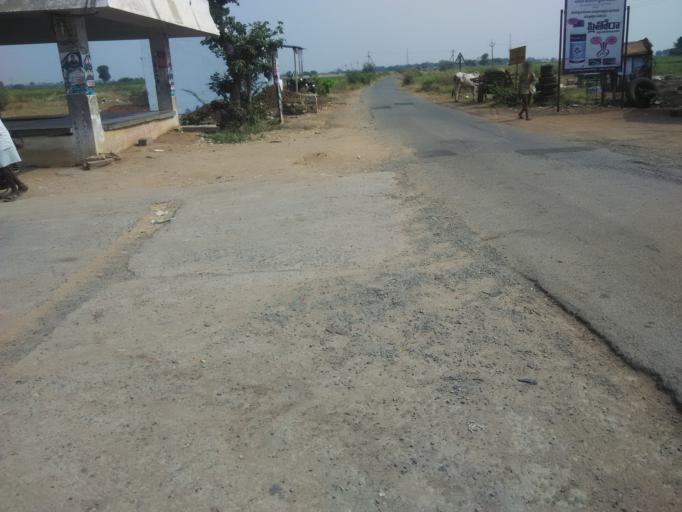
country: IN
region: Andhra Pradesh
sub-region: Kurnool
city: Nandyal
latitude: 15.4466
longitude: 78.4231
